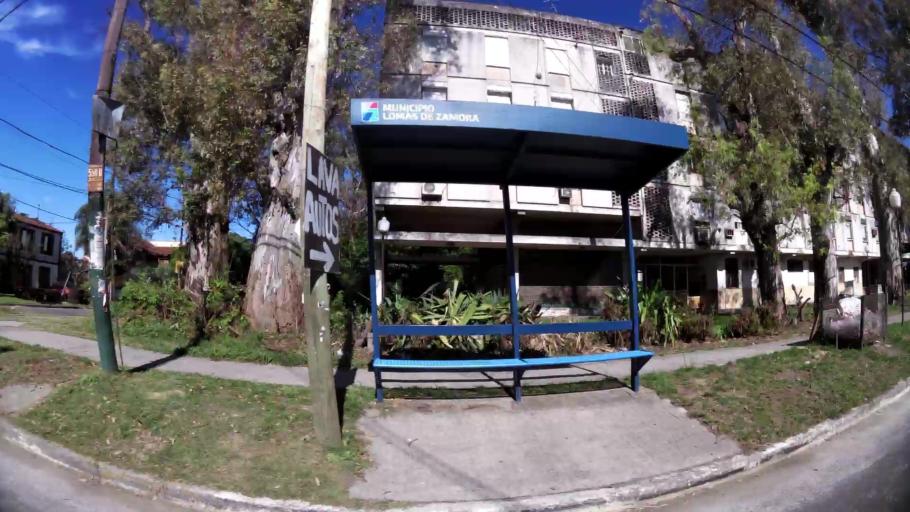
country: AR
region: Buenos Aires
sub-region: Partido de Lomas de Zamora
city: Lomas de Zamora
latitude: -34.7627
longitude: -58.4226
